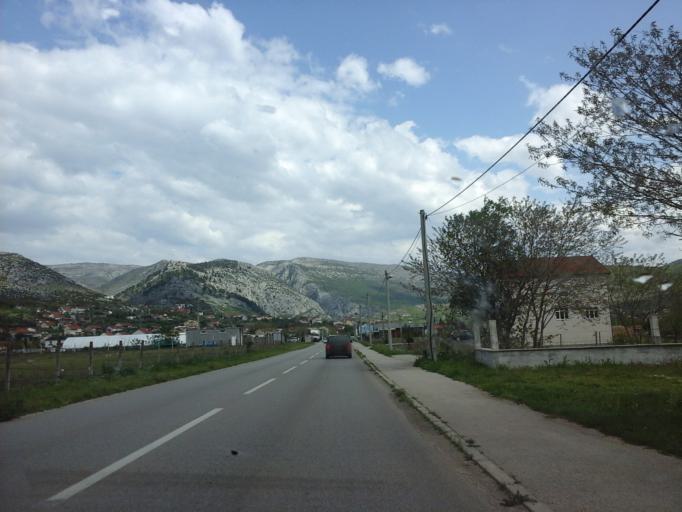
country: BA
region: Federation of Bosnia and Herzegovina
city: Blagaj
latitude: 43.2647
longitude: 17.8763
